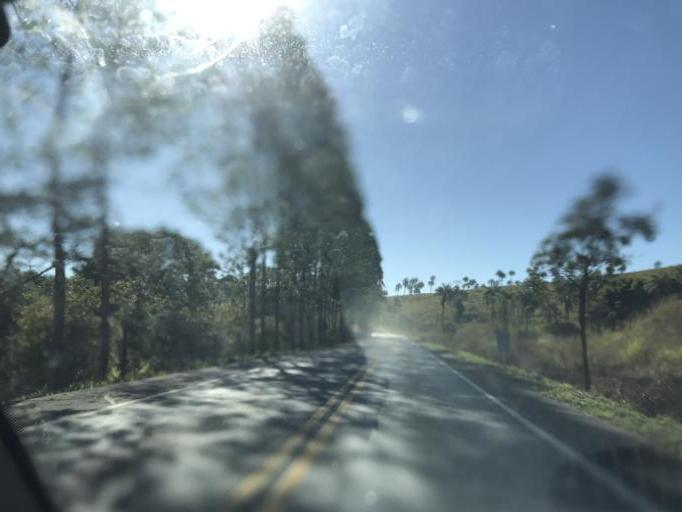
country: BR
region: Minas Gerais
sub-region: Bambui
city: Bambui
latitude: -19.8203
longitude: -46.0195
